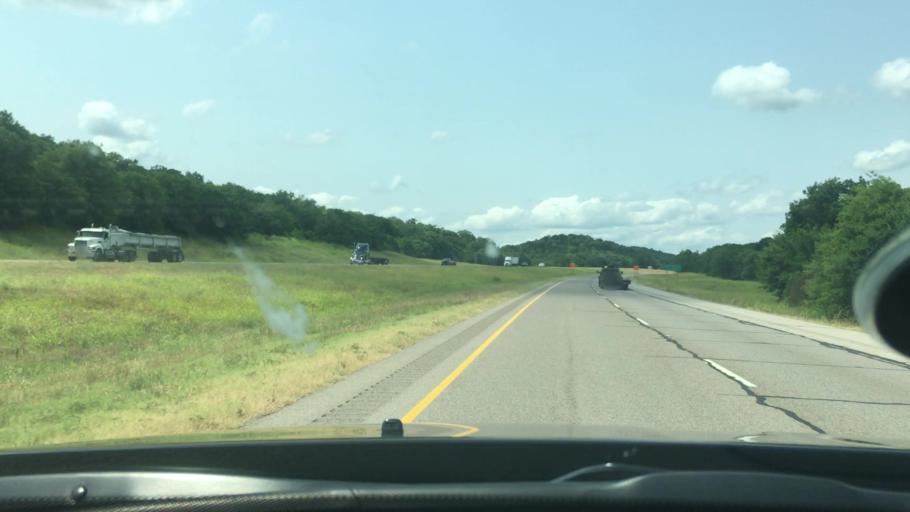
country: US
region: Oklahoma
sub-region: Murray County
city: Davis
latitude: 34.4673
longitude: -97.1511
